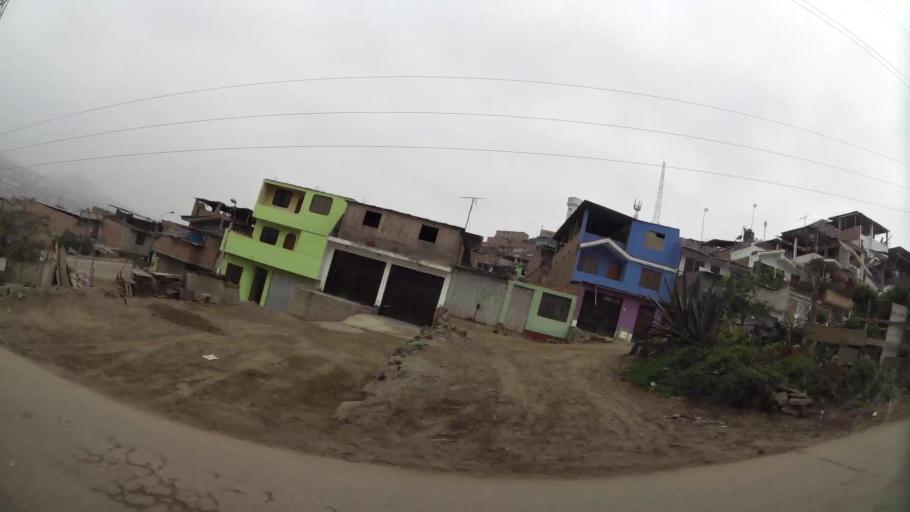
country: PE
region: Lima
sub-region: Lima
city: Surco
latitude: -12.1834
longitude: -76.9516
